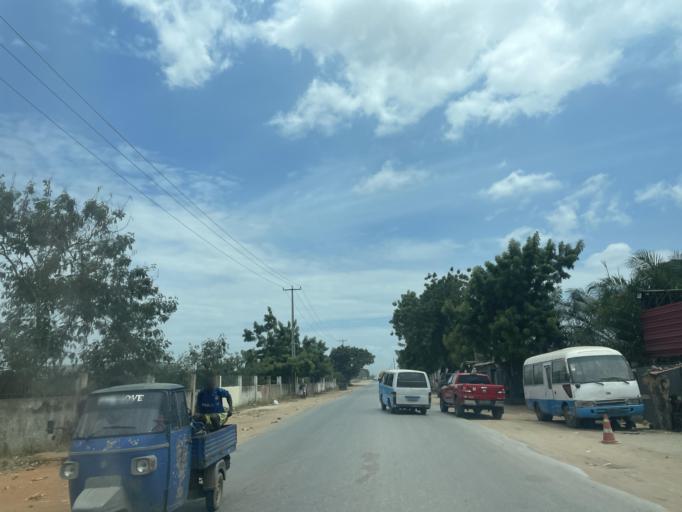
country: AO
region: Luanda
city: Luanda
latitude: -8.9325
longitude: 13.3813
